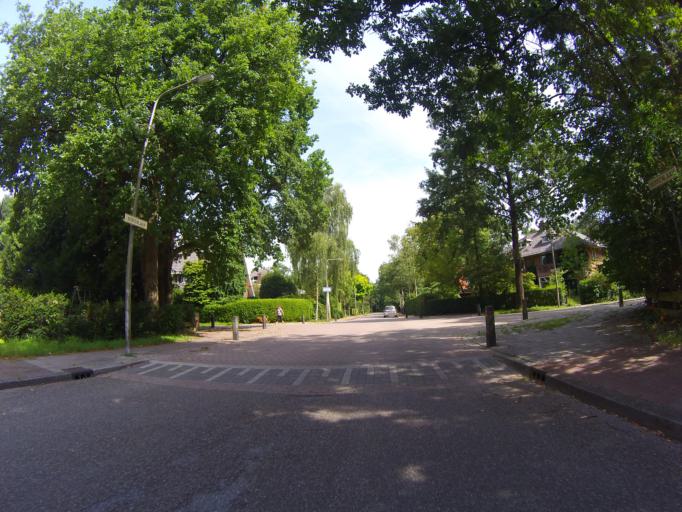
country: NL
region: Utrecht
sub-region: Gemeente Zeist
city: Zeist
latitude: 52.0954
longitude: 5.2482
